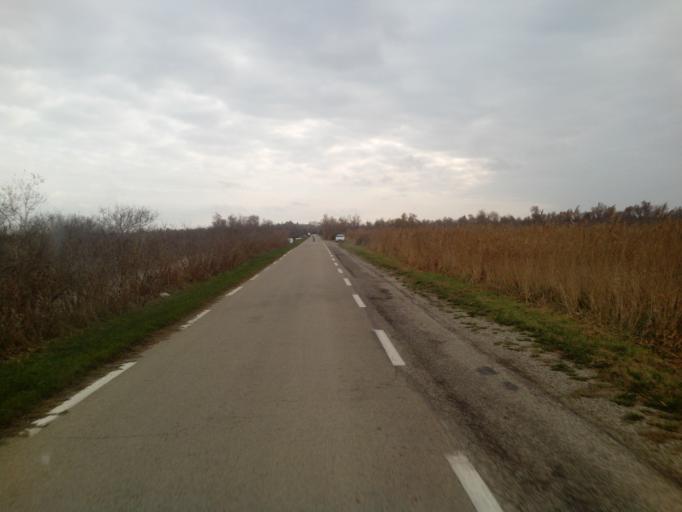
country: FR
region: Languedoc-Roussillon
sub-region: Departement du Gard
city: Vauvert
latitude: 43.6106
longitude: 4.3308
